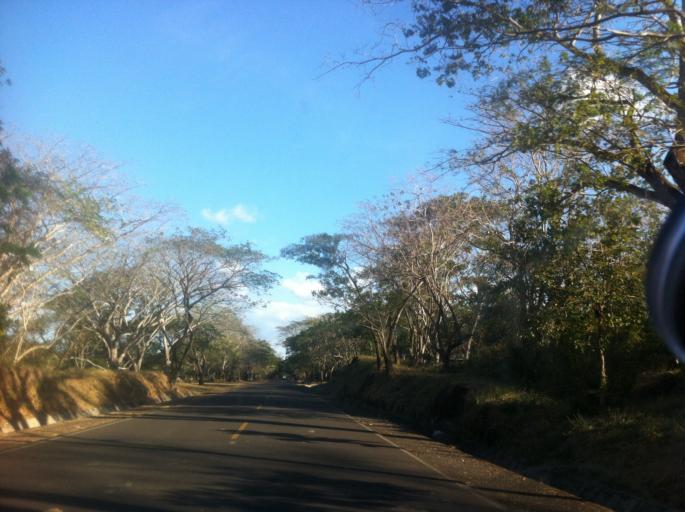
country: NI
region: Rio San Juan
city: Morrito
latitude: 11.7089
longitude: -84.9528
